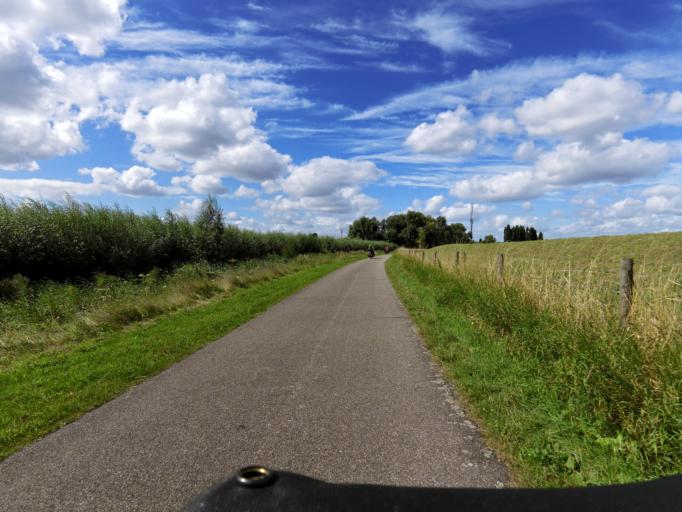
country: NL
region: South Holland
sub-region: Gemeente Zwijndrecht
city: Heerjansdam
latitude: 51.8272
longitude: 4.5598
